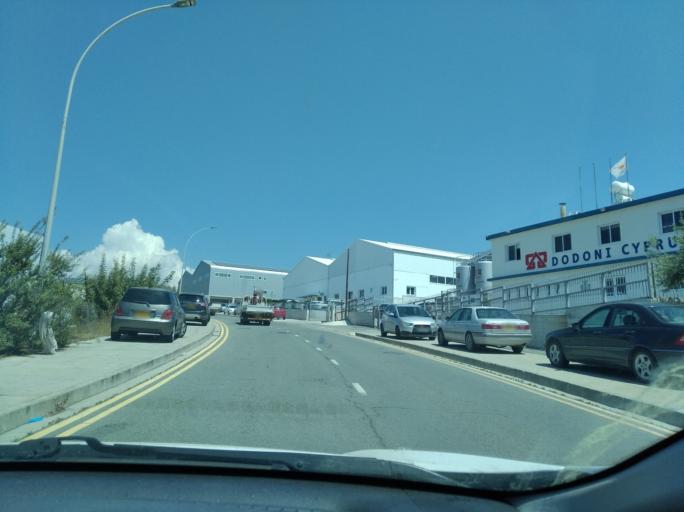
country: CY
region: Limassol
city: Ypsonas
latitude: 34.7308
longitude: 32.9434
